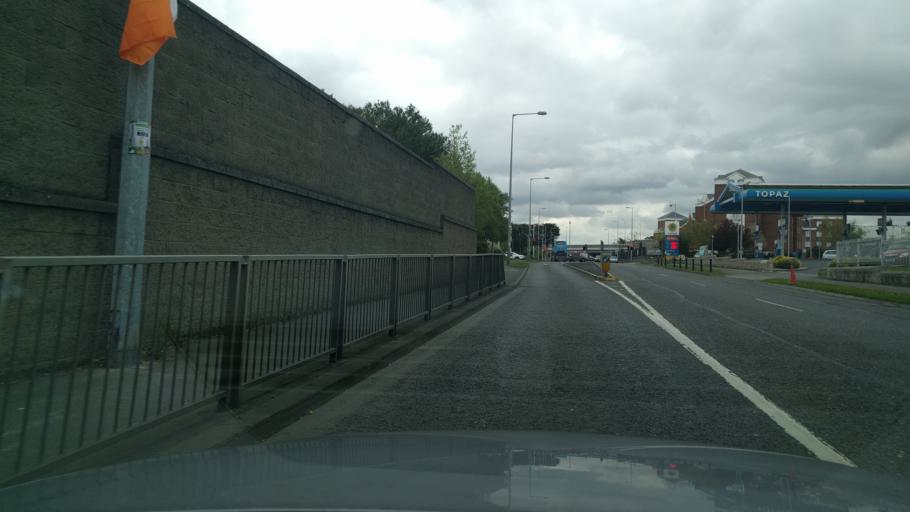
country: IE
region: Leinster
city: Clondalkin
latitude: 53.3152
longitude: -6.3945
